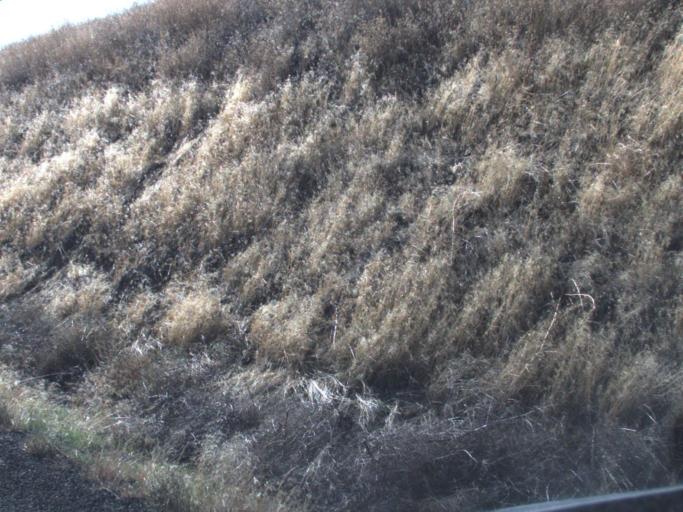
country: US
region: Washington
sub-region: Walla Walla County
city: Waitsburg
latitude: 46.2758
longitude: -118.3468
